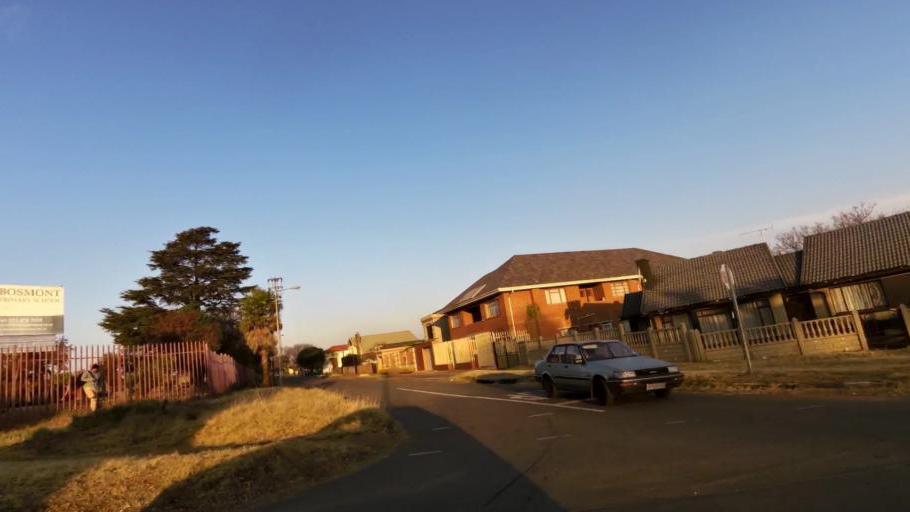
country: ZA
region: Gauteng
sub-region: City of Johannesburg Metropolitan Municipality
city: Roodepoort
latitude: -26.1854
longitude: 27.9495
